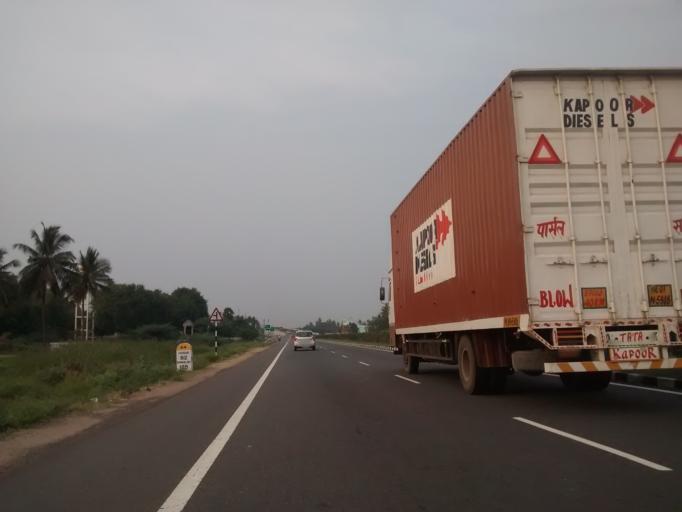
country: IN
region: Tamil Nadu
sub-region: Dharmapuri
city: Dharmapuri
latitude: 12.2373
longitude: 78.1950
